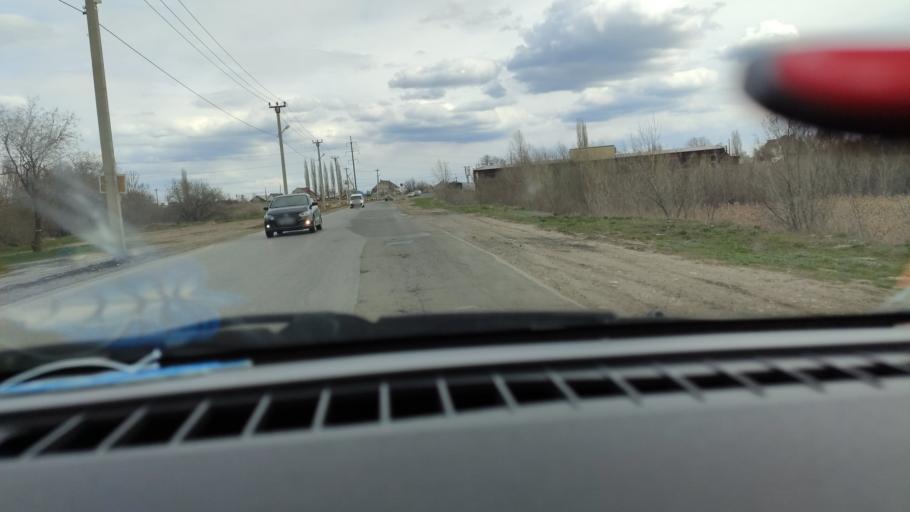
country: RU
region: Saratov
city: Engel's
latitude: 51.4602
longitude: 46.0909
